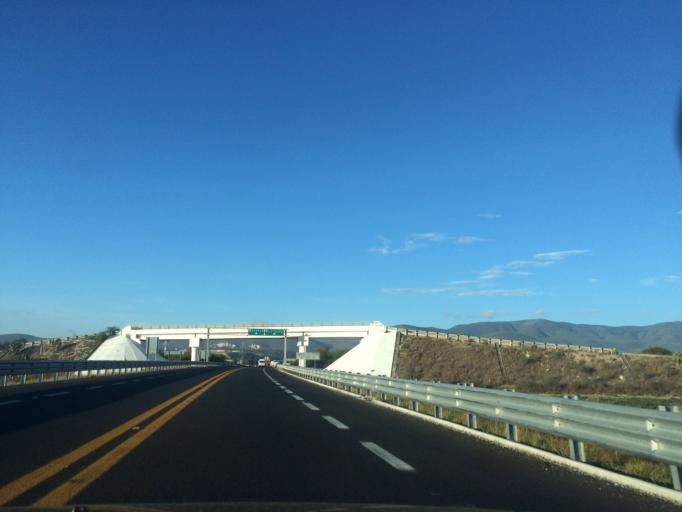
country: MX
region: Puebla
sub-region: Santiago Miahuatlan
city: San Jose Monte Chiquito
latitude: 18.4936
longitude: -97.4547
